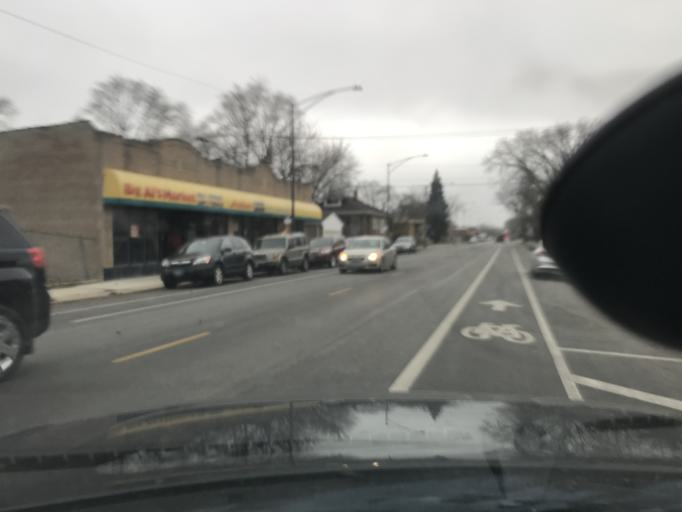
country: US
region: Indiana
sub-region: Lake County
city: Whiting
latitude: 41.7446
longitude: -87.5686
